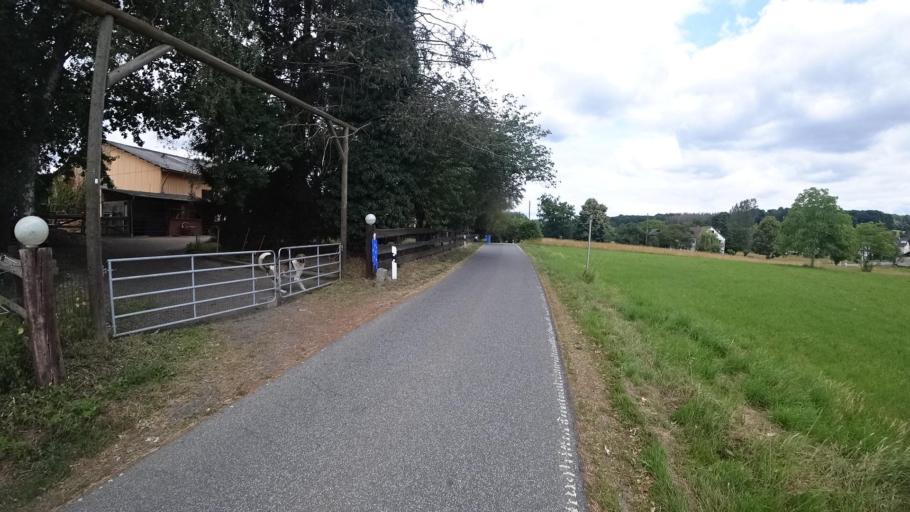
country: DE
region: Rheinland-Pfalz
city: Werkhausen
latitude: 50.7204
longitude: 7.5314
